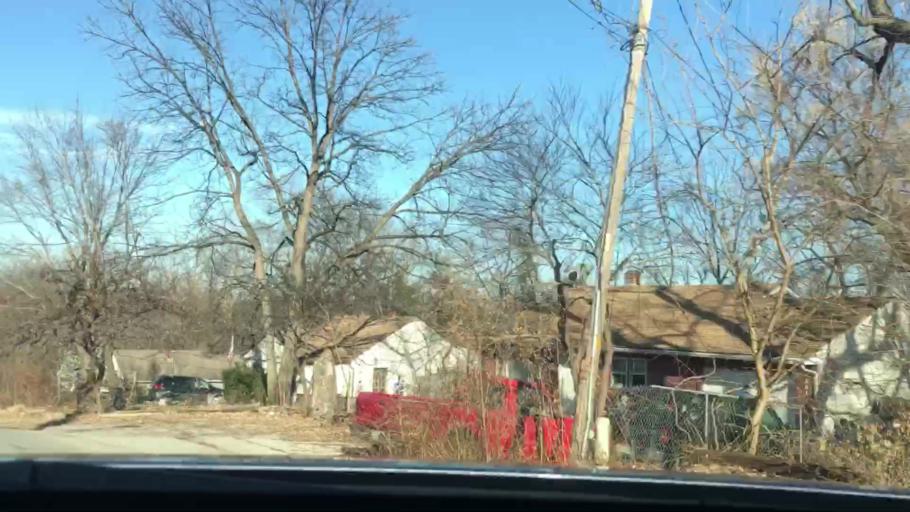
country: US
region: Missouri
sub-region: Platte County
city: Parkville
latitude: 39.2031
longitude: -94.6872
